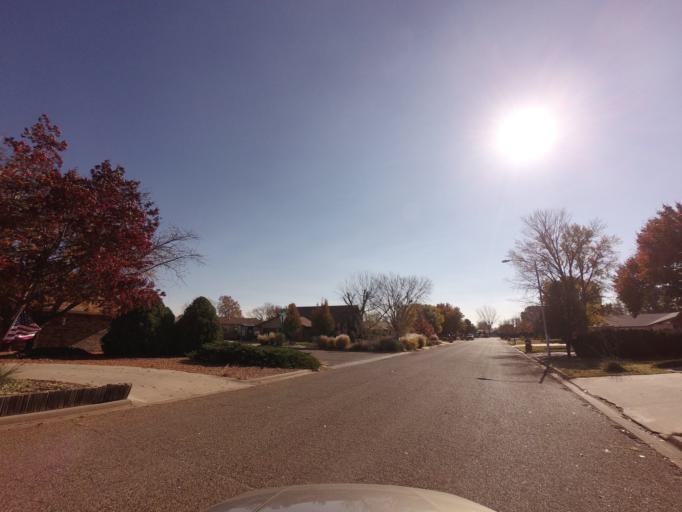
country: US
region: New Mexico
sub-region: Curry County
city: Clovis
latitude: 34.4142
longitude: -103.1832
